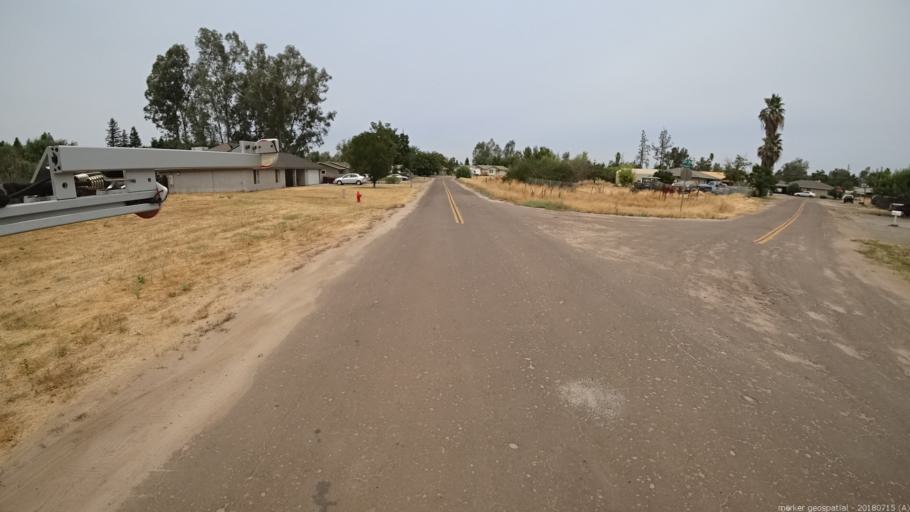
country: US
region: California
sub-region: Madera County
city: Madera Acres
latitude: 37.0094
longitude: -120.0821
